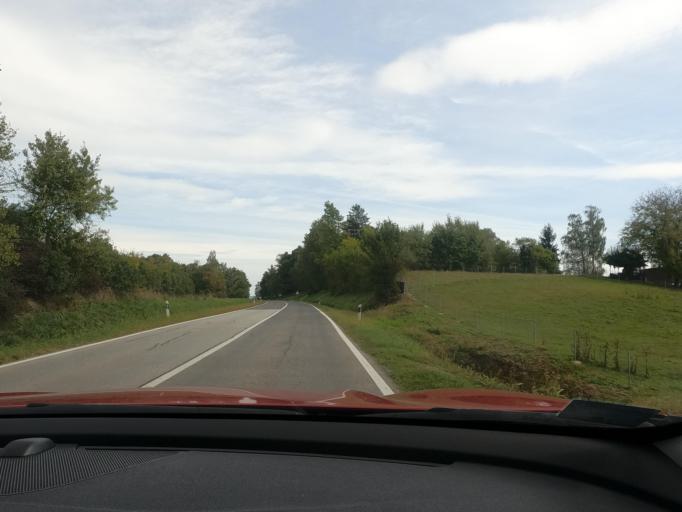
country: HR
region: Sisacko-Moslavacka
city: Osekovo
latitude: 45.5332
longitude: 16.5618
